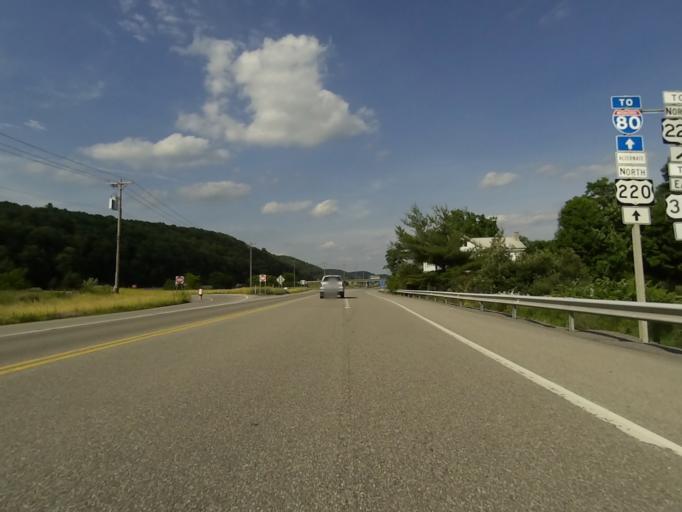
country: US
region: Pennsylvania
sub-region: Centre County
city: Stormstown
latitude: 40.8273
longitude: -78.0206
